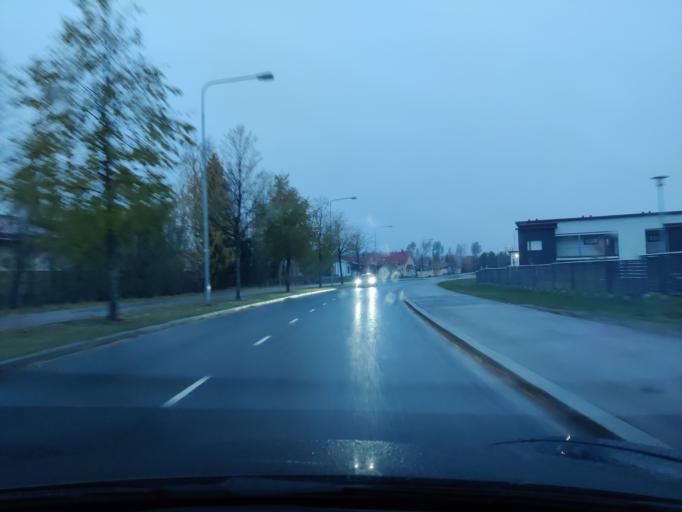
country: FI
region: Northern Savo
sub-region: Kuopio
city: Kuopio
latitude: 62.8258
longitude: 27.6953
